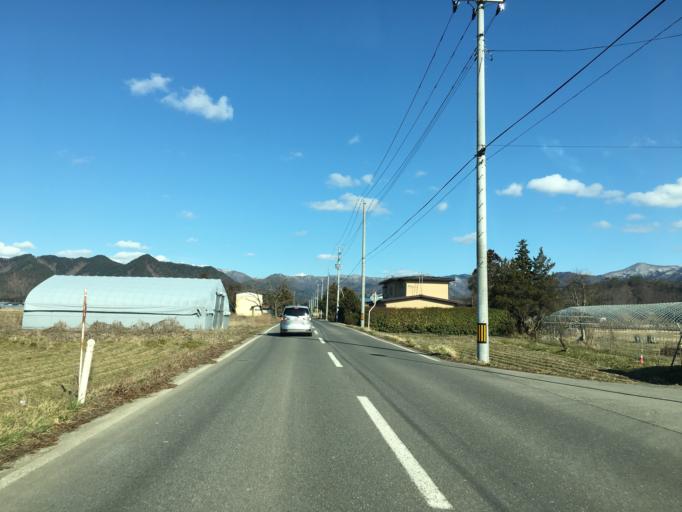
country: JP
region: Yamagata
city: Takahata
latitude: 37.9534
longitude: 140.1701
